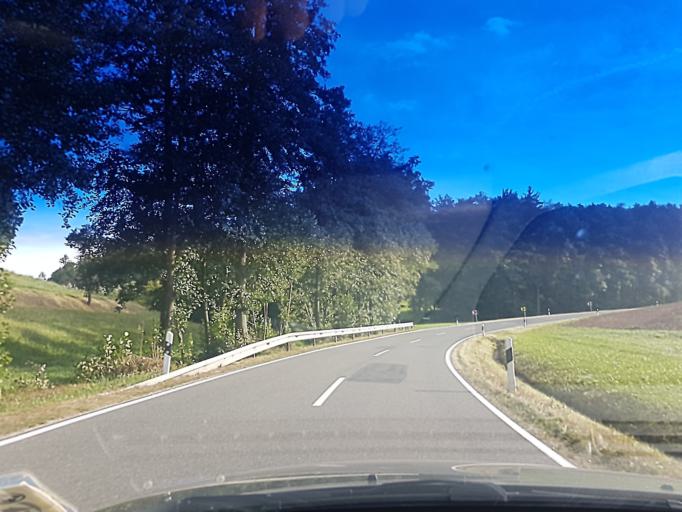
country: DE
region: Bavaria
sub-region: Upper Franconia
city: Burgwindheim
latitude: 49.8081
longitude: 10.5840
